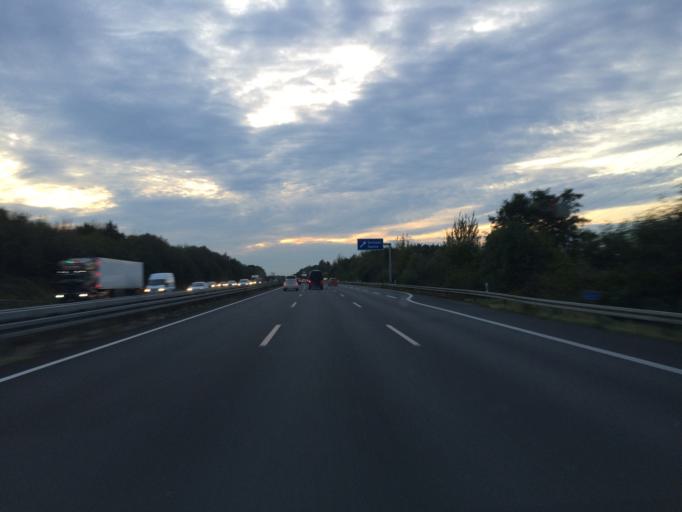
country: DE
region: Lower Saxony
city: Garbsen
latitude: 52.4236
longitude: 9.5825
